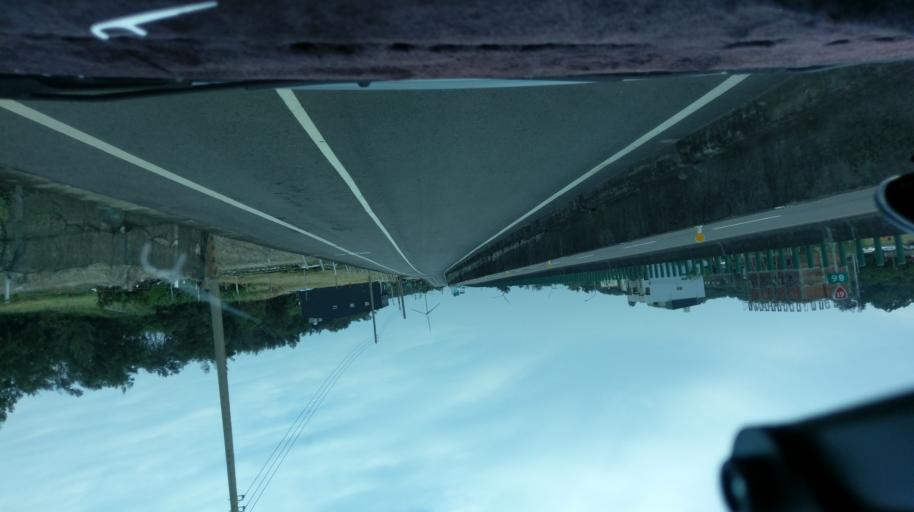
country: TW
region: Taiwan
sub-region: Hsinchu
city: Hsinchu
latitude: 24.7329
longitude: 120.8799
